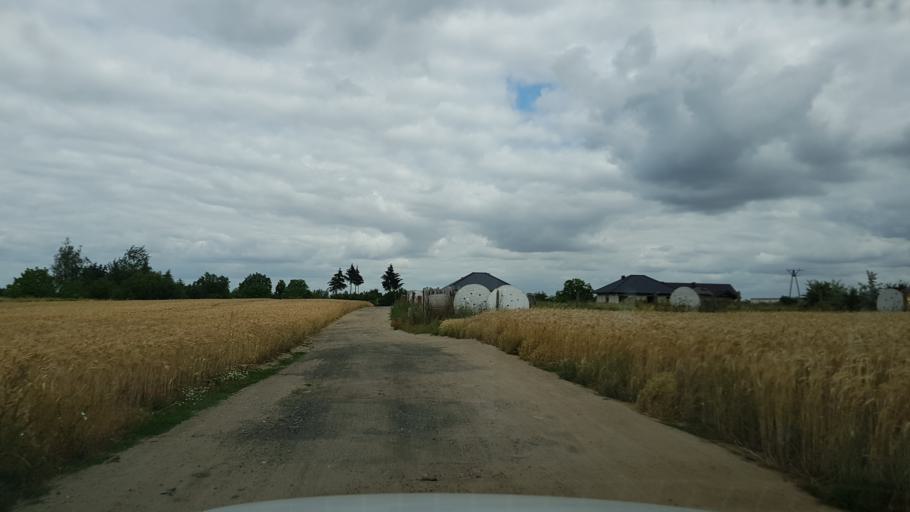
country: PL
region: West Pomeranian Voivodeship
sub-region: Powiat mysliborski
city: Mysliborz
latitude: 52.9318
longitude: 14.8765
